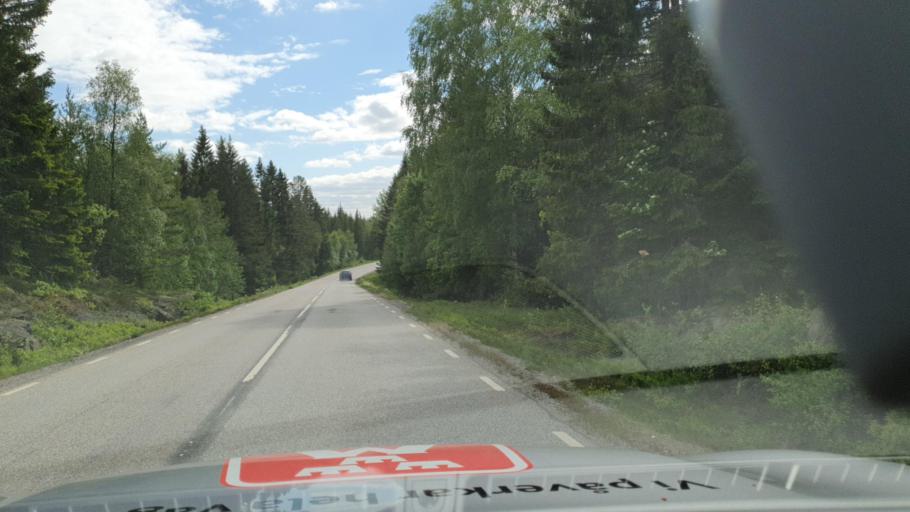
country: SE
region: Vaesternorrland
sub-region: Kramfors Kommun
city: Nordingra
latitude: 62.9098
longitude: 18.1610
